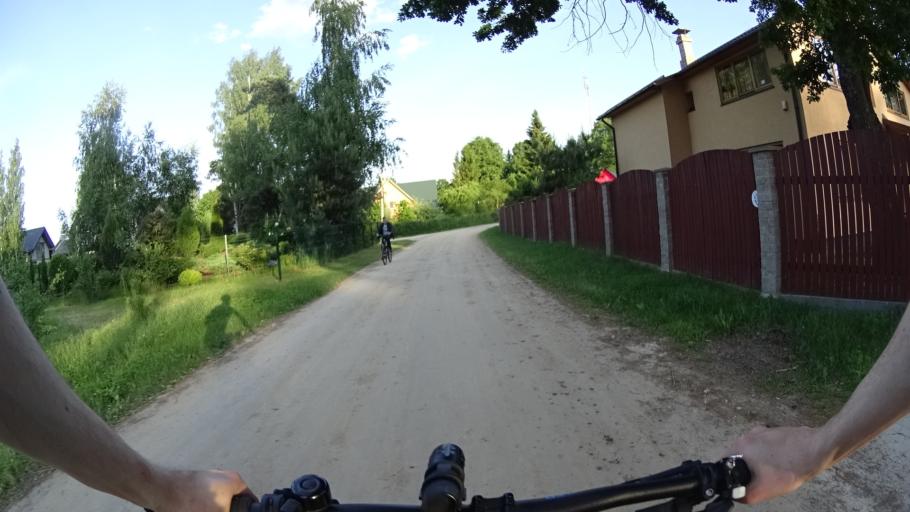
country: LV
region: Riga
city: Jaunciems
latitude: 57.1030
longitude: 24.1937
